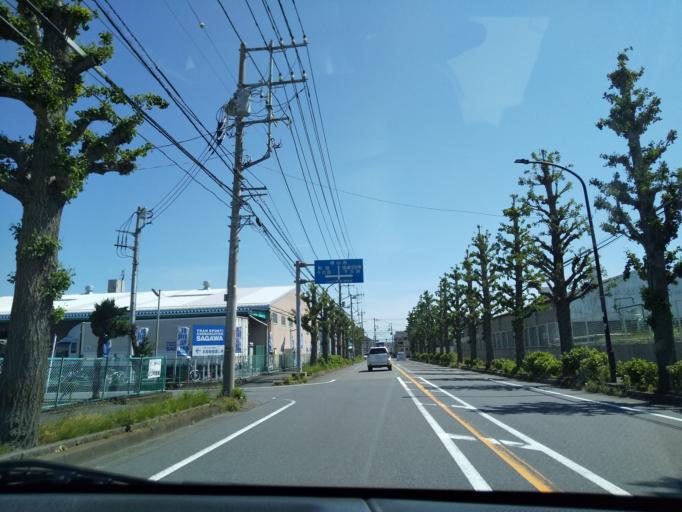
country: JP
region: Tokyo
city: Hachioji
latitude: 35.5723
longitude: 139.3545
